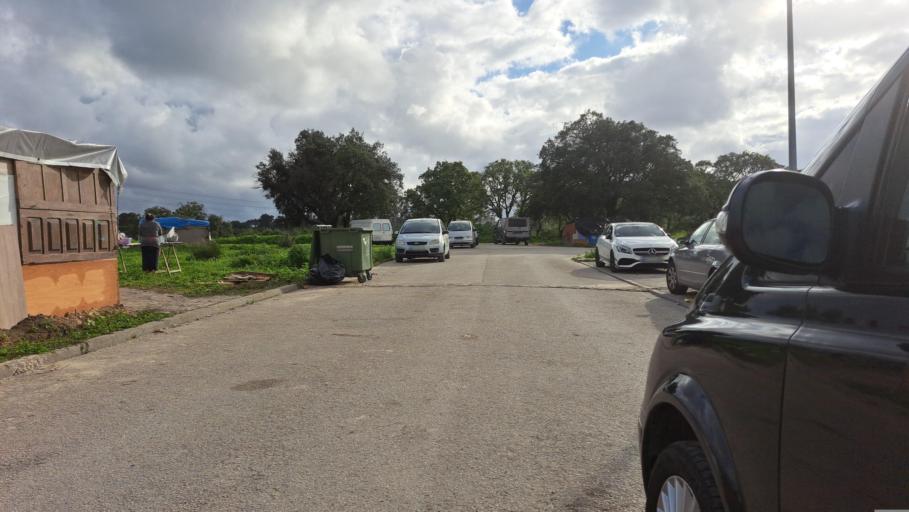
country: PT
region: Setubal
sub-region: Moita
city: Alhos Vedros
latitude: 38.6441
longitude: -9.0339
